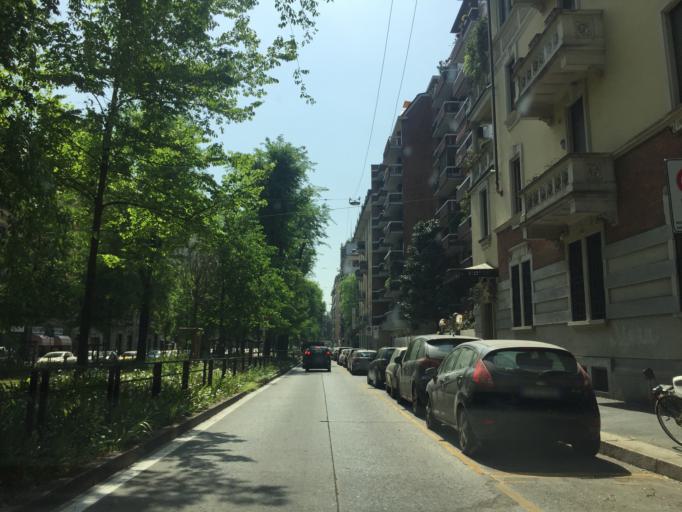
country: IT
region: Lombardy
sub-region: Citta metropolitana di Milano
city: Milano
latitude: 45.4901
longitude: 9.1628
